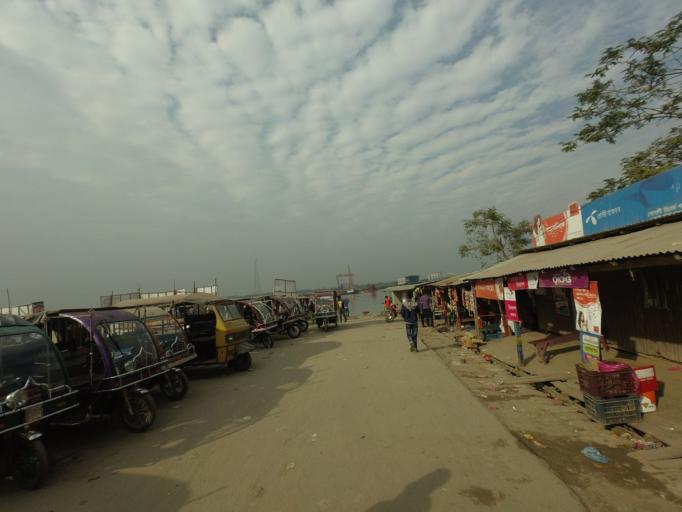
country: BD
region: Barisal
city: Nalchiti
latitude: 22.4633
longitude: 90.3415
